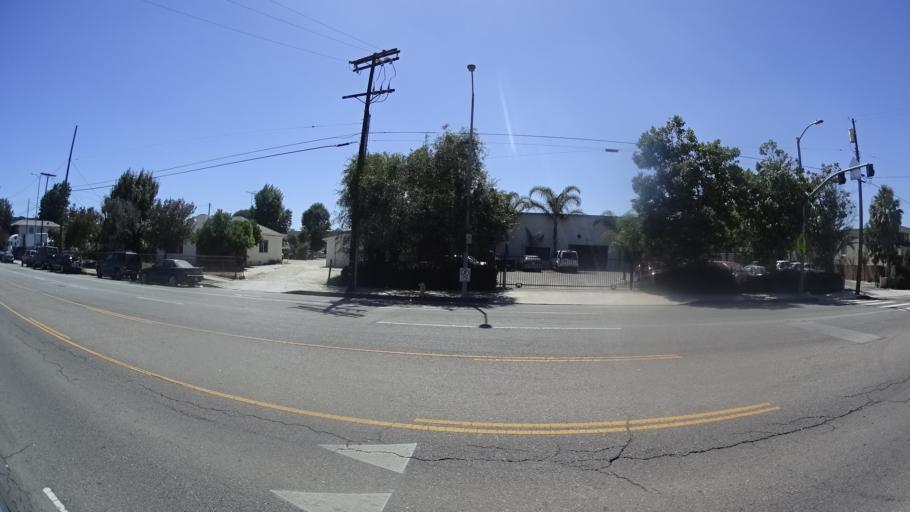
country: US
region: California
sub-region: Los Angeles County
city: Van Nuys
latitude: 34.1959
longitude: -118.4837
